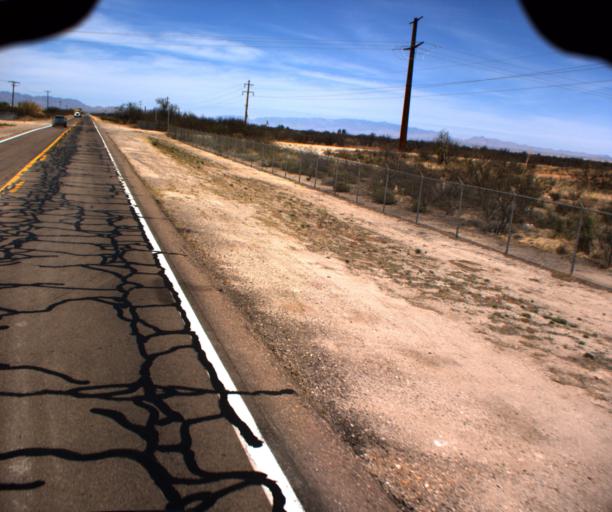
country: US
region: Arizona
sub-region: Cochise County
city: Willcox
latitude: 32.0635
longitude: -109.8928
